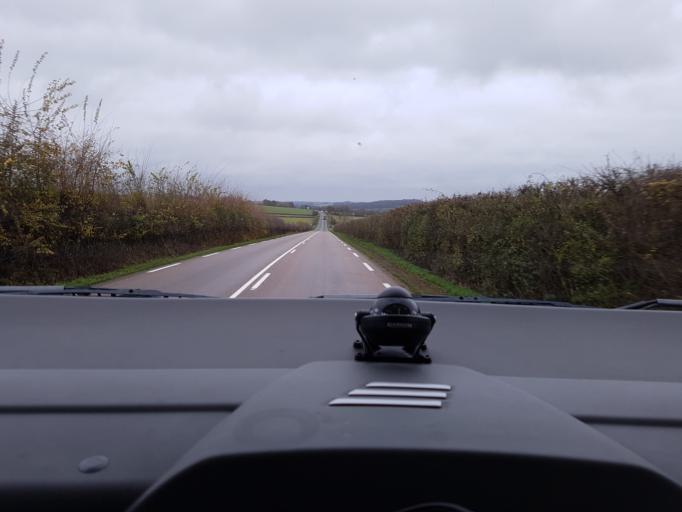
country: FR
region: Picardie
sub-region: Departement de l'Oise
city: Songeons
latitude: 49.5200
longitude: 1.8280
